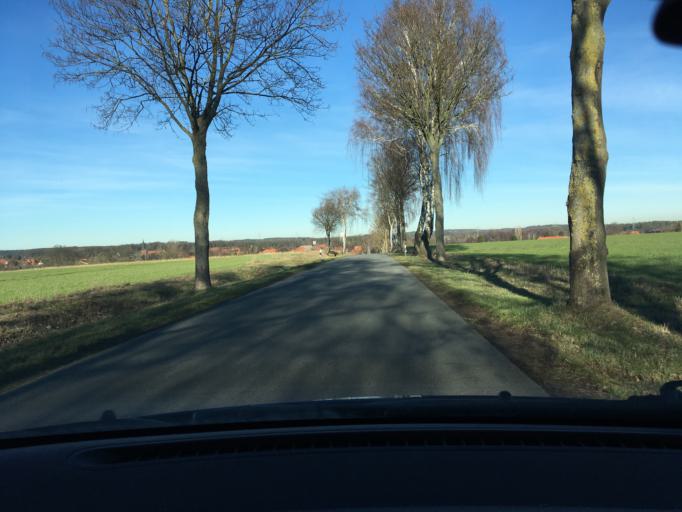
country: DE
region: Lower Saxony
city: Hanstedt Eins
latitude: 53.0388
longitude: 10.3723
